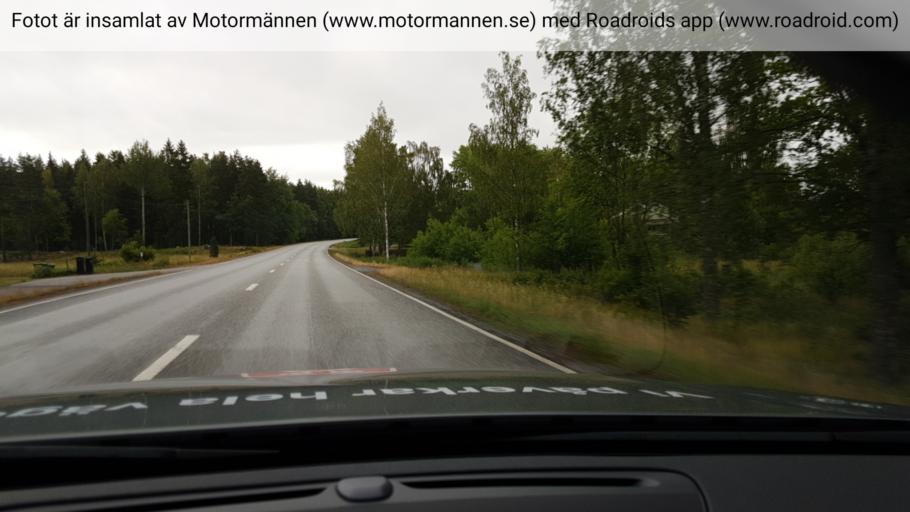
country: SE
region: Vaestmanland
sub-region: Kungsors Kommun
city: Kungsoer
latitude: 59.2986
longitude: 16.2136
